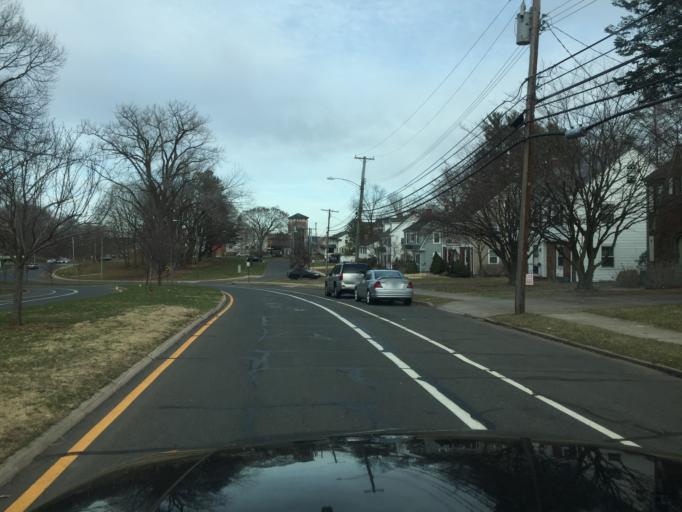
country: US
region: Connecticut
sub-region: Hartford County
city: New Britain
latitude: 41.6914
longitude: -72.7739
